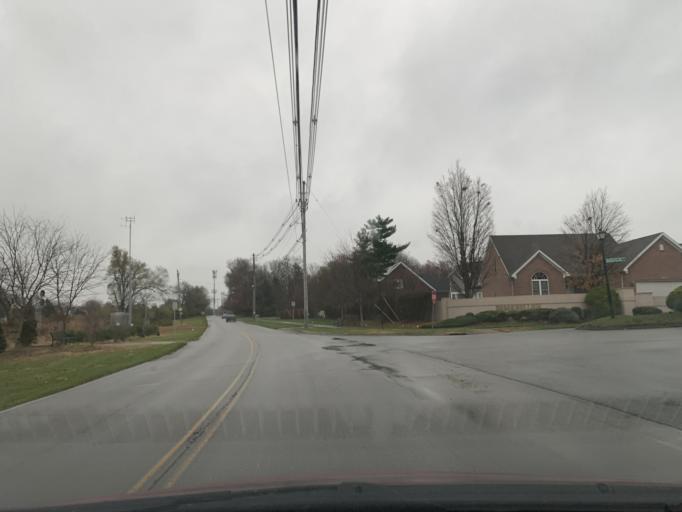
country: US
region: Kentucky
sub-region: Jefferson County
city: Saint Regis Park
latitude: 38.1992
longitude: -85.6099
